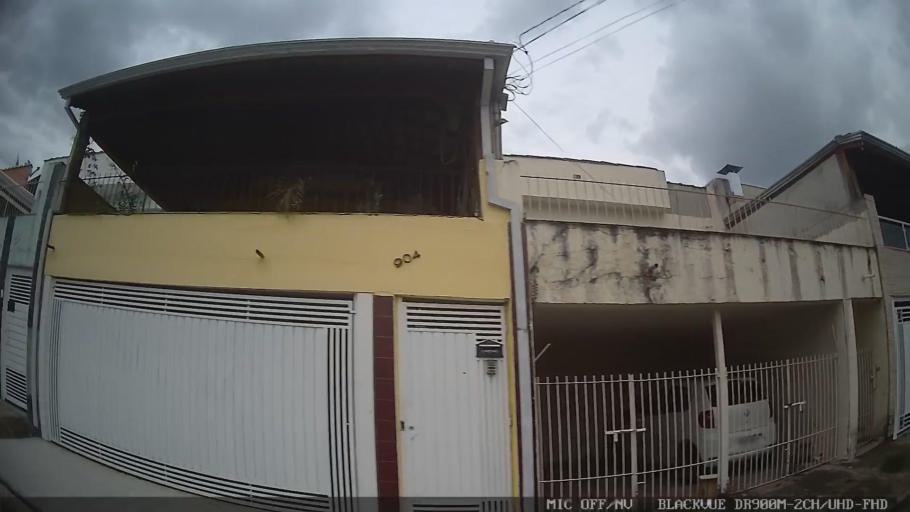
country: BR
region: Sao Paulo
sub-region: Atibaia
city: Atibaia
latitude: -23.1281
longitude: -46.5577
